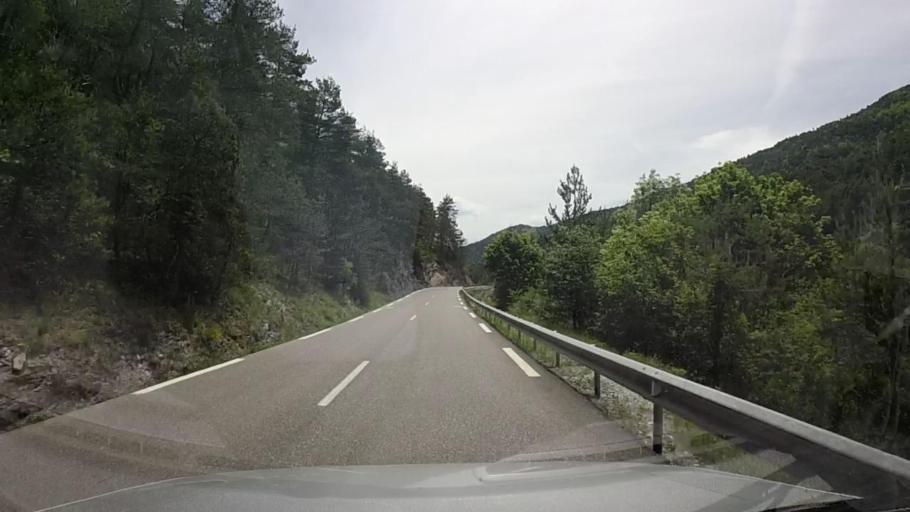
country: FR
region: Provence-Alpes-Cote d'Azur
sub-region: Departement des Alpes-de-Haute-Provence
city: Le Brusquet
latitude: 44.2211
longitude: 6.3605
